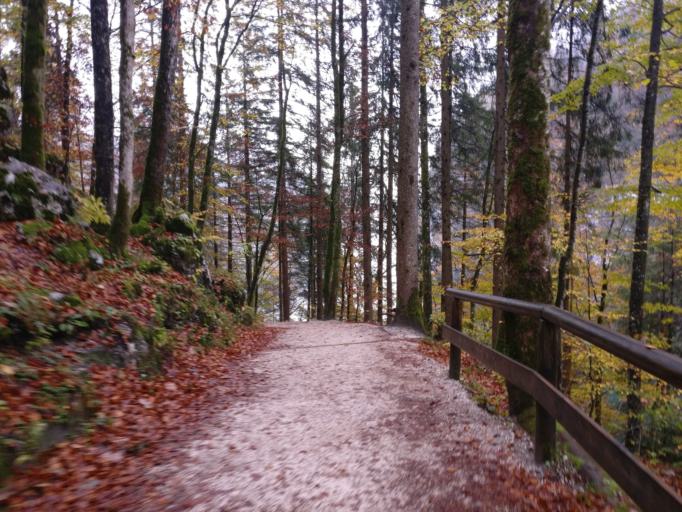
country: DE
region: Bavaria
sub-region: Upper Bavaria
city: Schoenau am Koenigssee
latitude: 47.5838
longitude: 12.9910
